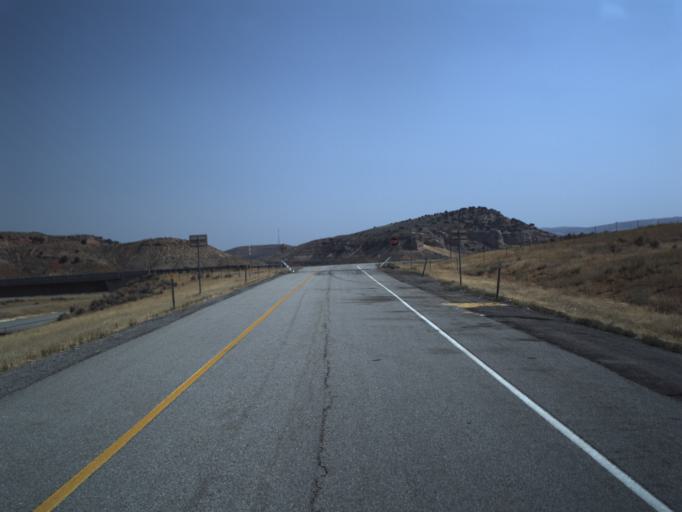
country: US
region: Wyoming
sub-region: Uinta County
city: Evanston
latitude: 41.1181
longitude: -111.1921
